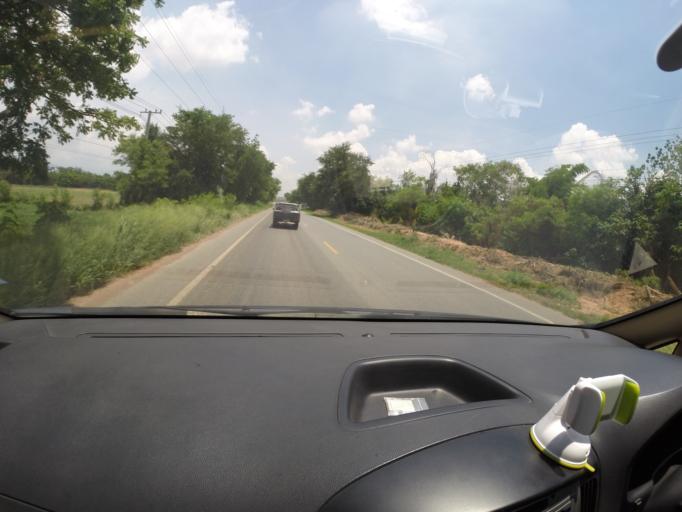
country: TH
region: Nakhon Ratchasima
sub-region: Amphoe Thepharak
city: Thepharak
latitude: 15.1274
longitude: 101.5545
